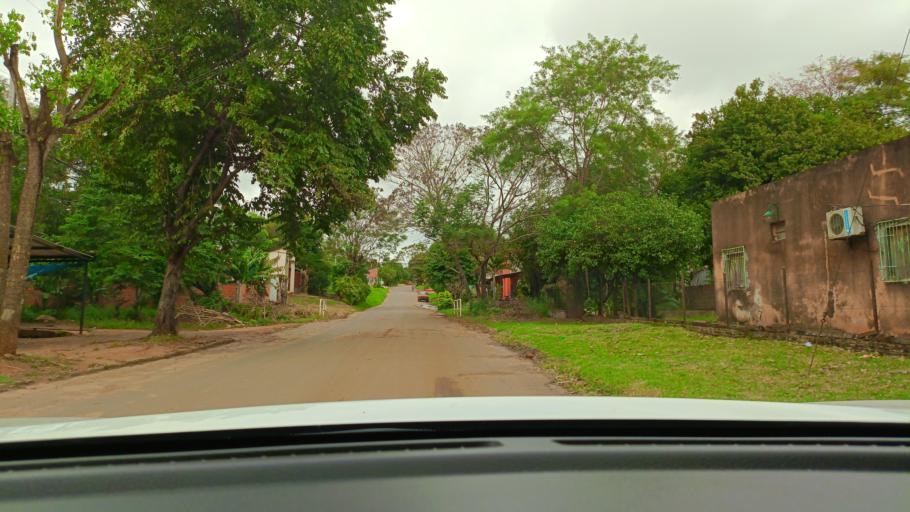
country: PY
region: San Pedro
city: Guayaybi
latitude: -24.6663
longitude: -56.4488
